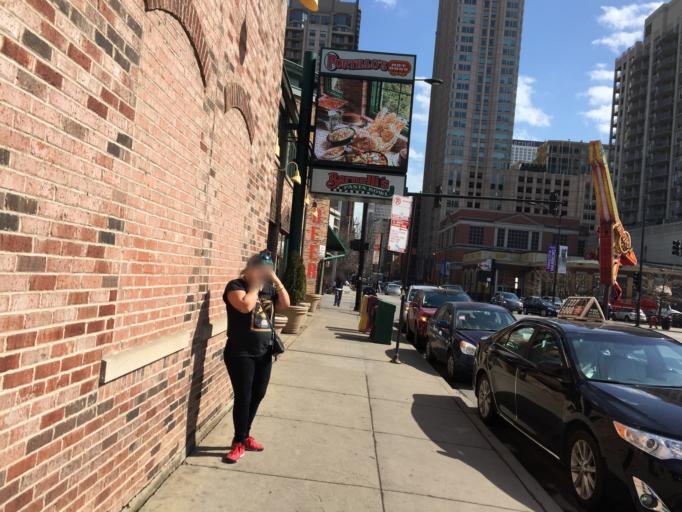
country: US
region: Illinois
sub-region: Cook County
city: Chicago
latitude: 41.8933
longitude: -87.6316
